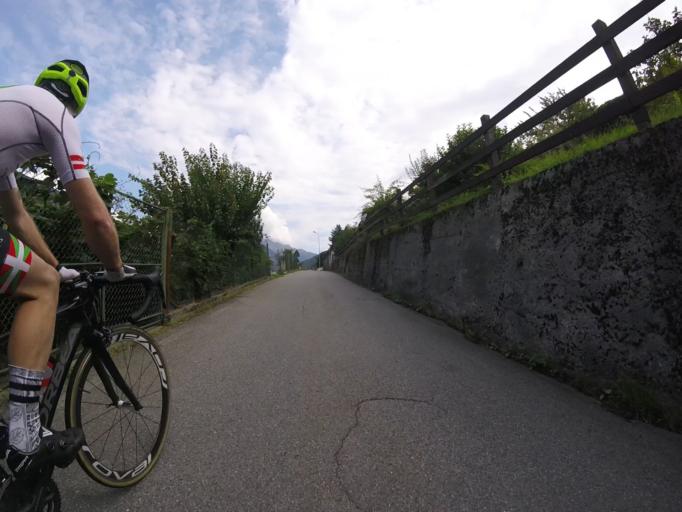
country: IT
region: Lombardy
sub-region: Provincia di Sondrio
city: Mazzo di Valtellina
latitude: 46.2514
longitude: 10.2560
